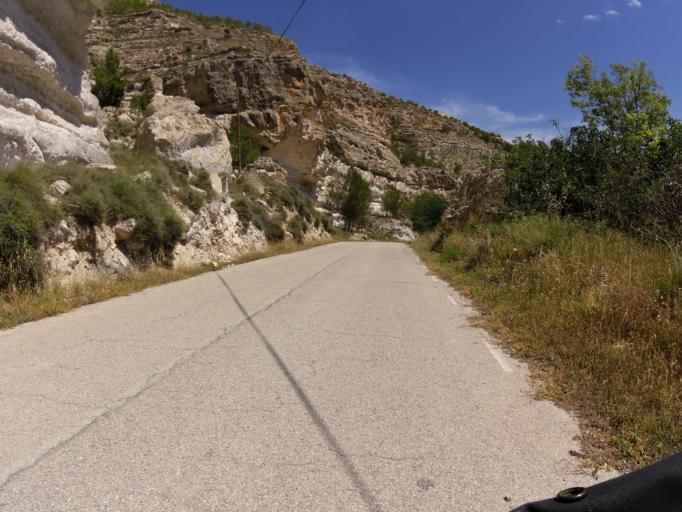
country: ES
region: Castille-La Mancha
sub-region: Provincia de Albacete
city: Jorquera
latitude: 39.1793
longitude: -1.5305
